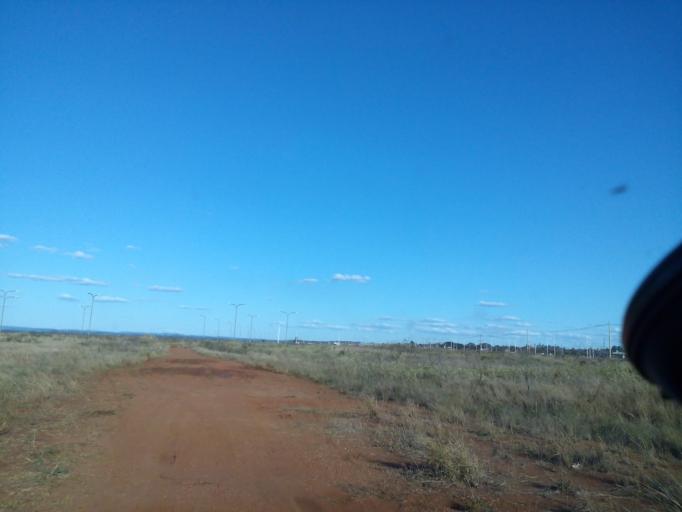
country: AR
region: Misiones
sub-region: Departamento de Capital
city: Posadas
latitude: -27.4118
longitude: -55.8873
